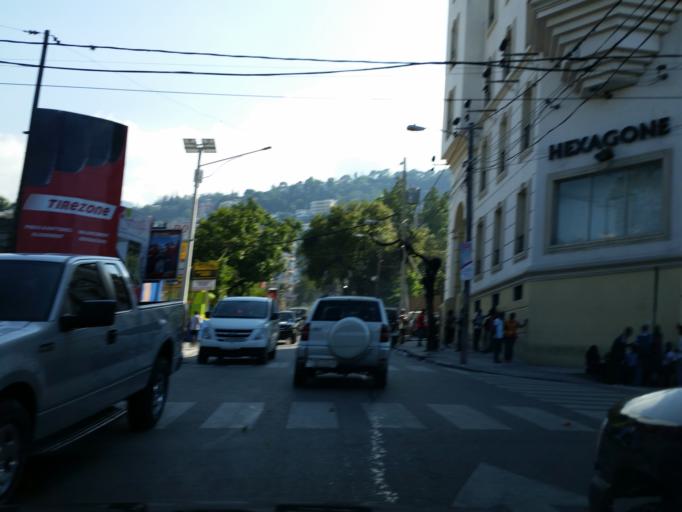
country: HT
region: Ouest
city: Petionville
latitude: 18.5138
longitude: -72.2897
